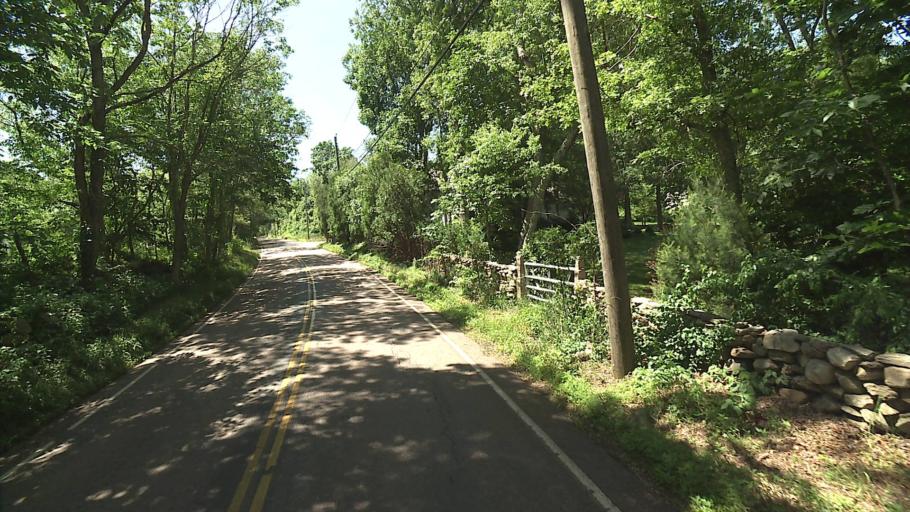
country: US
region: Rhode Island
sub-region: Washington County
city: Ashaway
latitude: 41.4510
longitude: -71.8456
